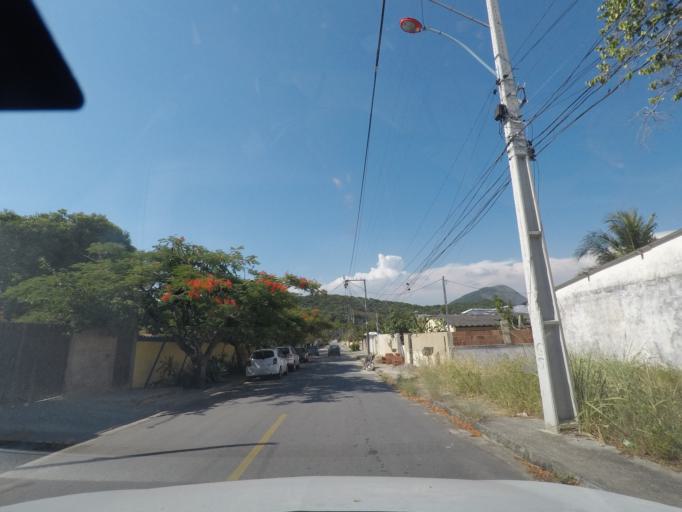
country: BR
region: Rio de Janeiro
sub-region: Niteroi
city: Niteroi
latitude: -22.9631
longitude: -42.9747
